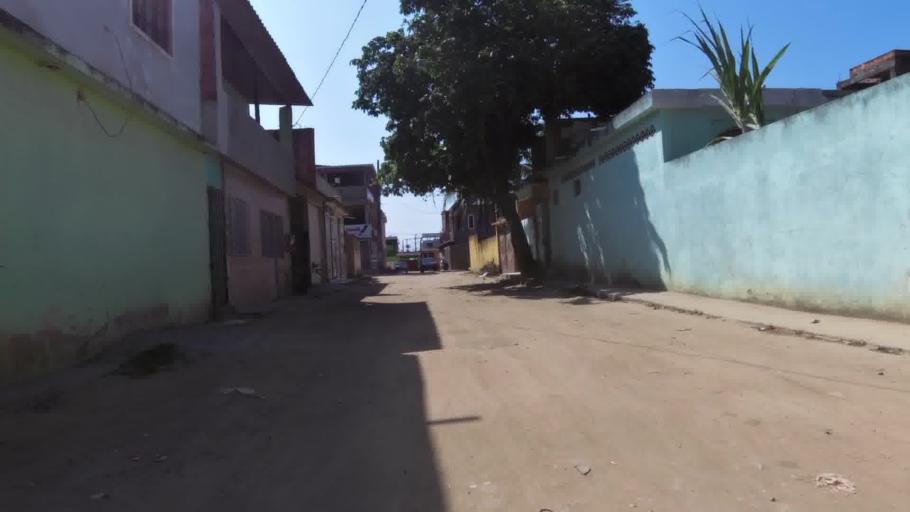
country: BR
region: Espirito Santo
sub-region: Itapemirim
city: Itapemirim
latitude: -21.0215
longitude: -40.8167
